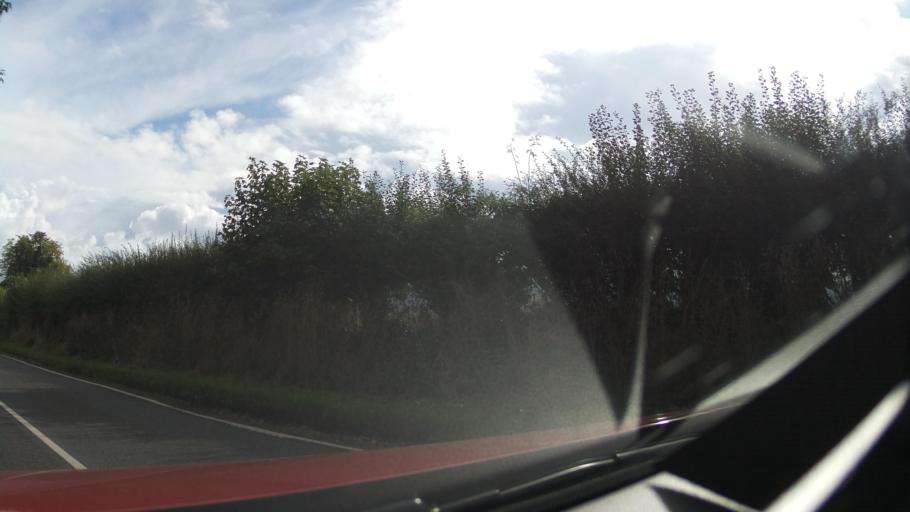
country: GB
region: England
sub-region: Telford and Wrekin
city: Madeley
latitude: 52.6253
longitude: -2.4125
